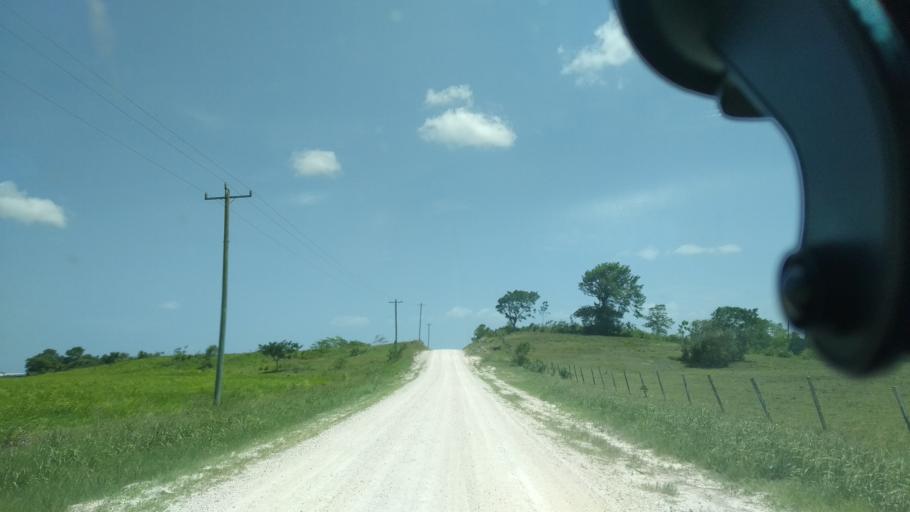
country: BZ
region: Cayo
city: San Ignacio
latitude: 17.3065
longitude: -89.0480
